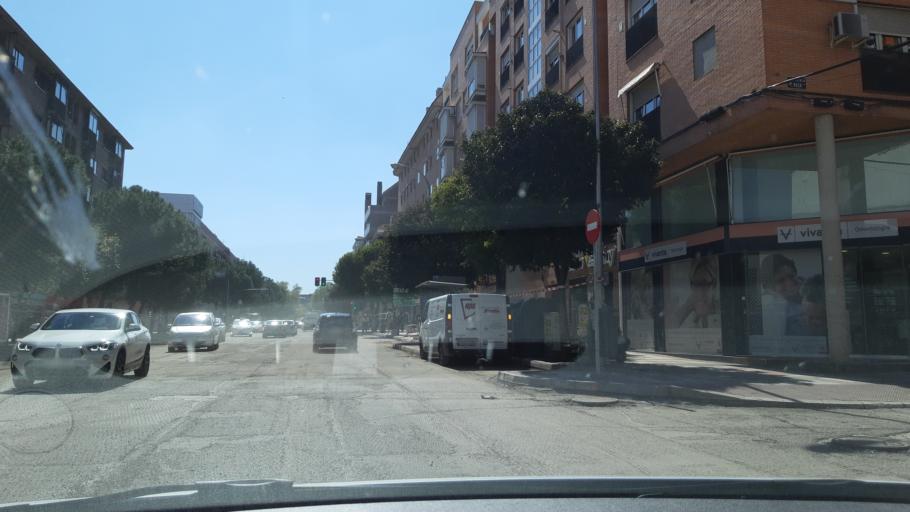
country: ES
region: Madrid
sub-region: Provincia de Madrid
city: San Blas
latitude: 40.4472
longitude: -3.6115
